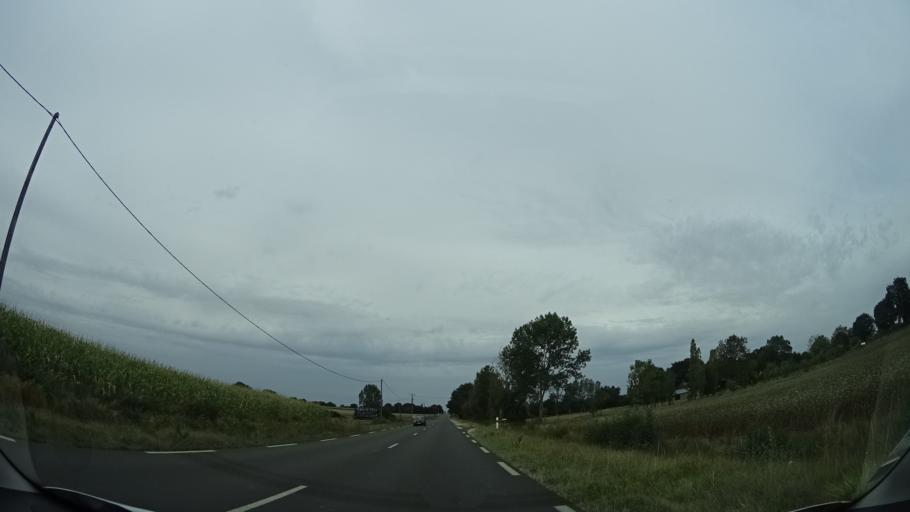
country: FR
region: Pays de la Loire
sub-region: Departement de la Mayenne
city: Meslay-du-Maine
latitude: 47.9594
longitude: -0.5703
